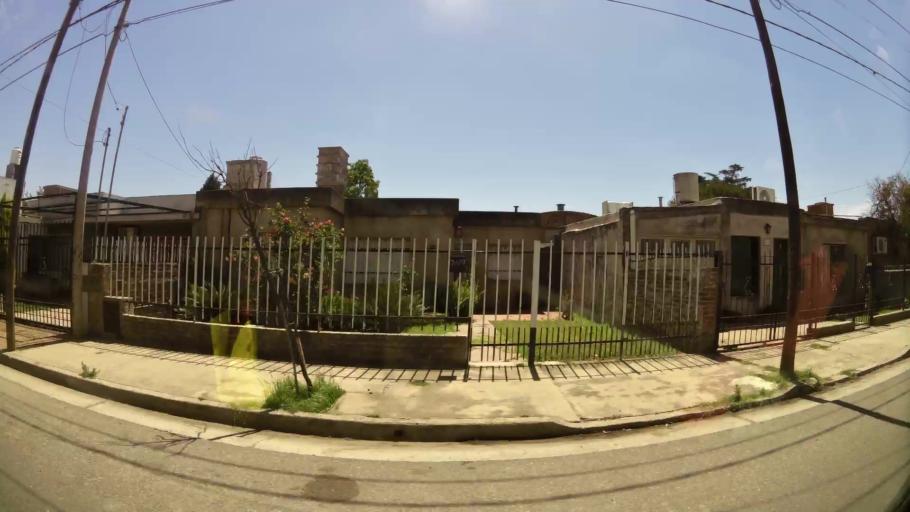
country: AR
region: Cordoba
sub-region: Departamento de Capital
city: Cordoba
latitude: -31.3786
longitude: -64.1567
